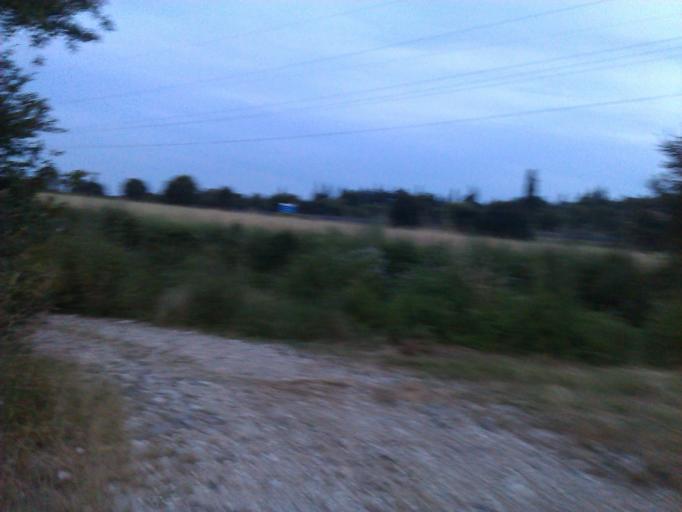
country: IT
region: Tuscany
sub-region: Province of Arezzo
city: Viciomaggio
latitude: 43.4439
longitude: 11.7729
